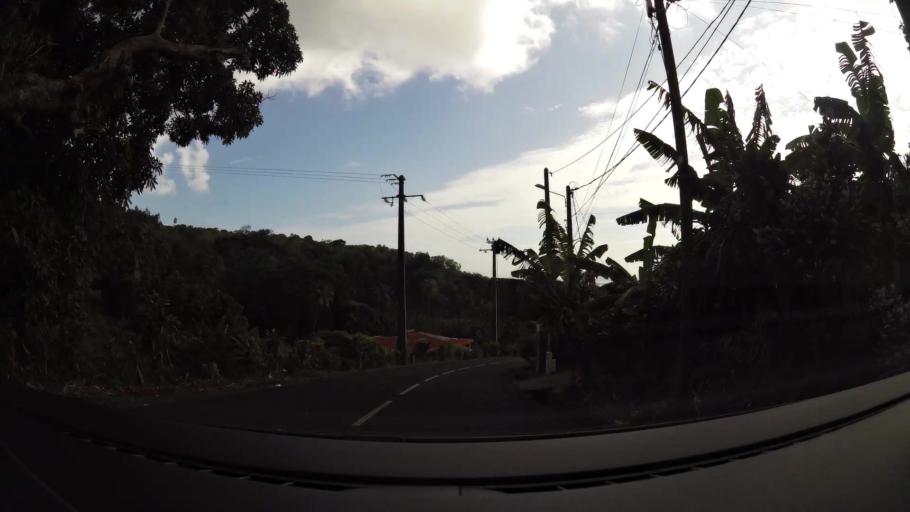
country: GP
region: Guadeloupe
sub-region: Guadeloupe
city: Trois-Rivieres
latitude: 15.9733
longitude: -61.6440
